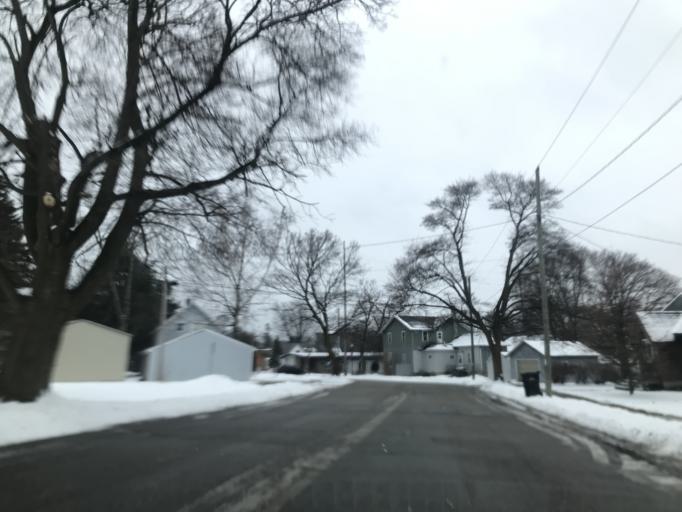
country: US
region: Wisconsin
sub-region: Door County
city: Sturgeon Bay
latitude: 44.8398
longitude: -87.3742
